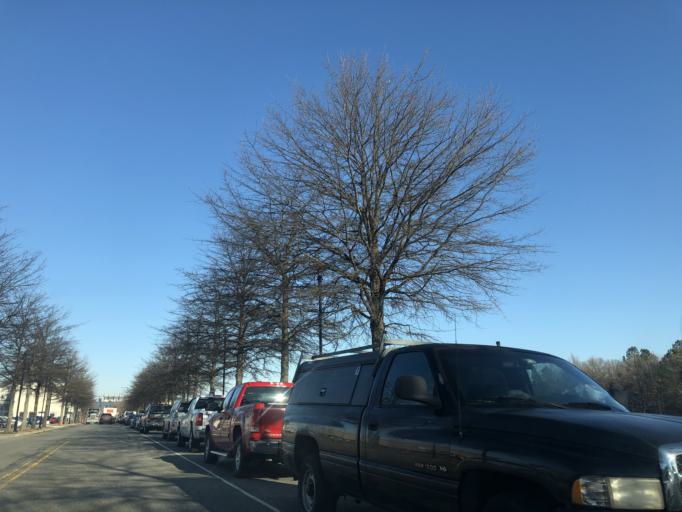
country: US
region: New Jersey
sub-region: Gloucester County
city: National Park
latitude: 39.8888
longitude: -75.1662
